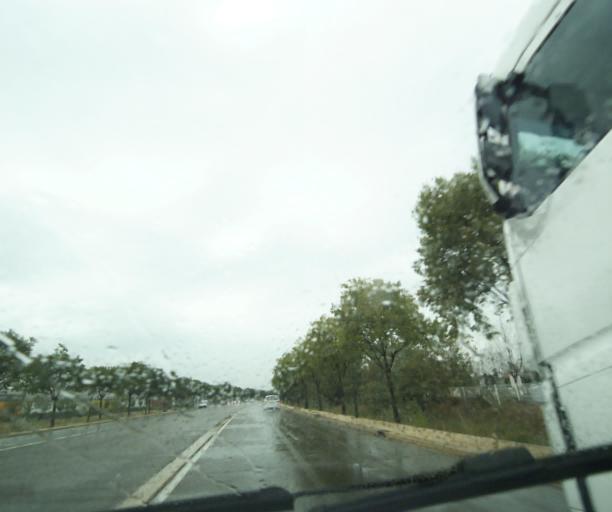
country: FR
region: Languedoc-Roussillon
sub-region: Departement du Gard
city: Caissargues
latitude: 43.8087
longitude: 4.3698
